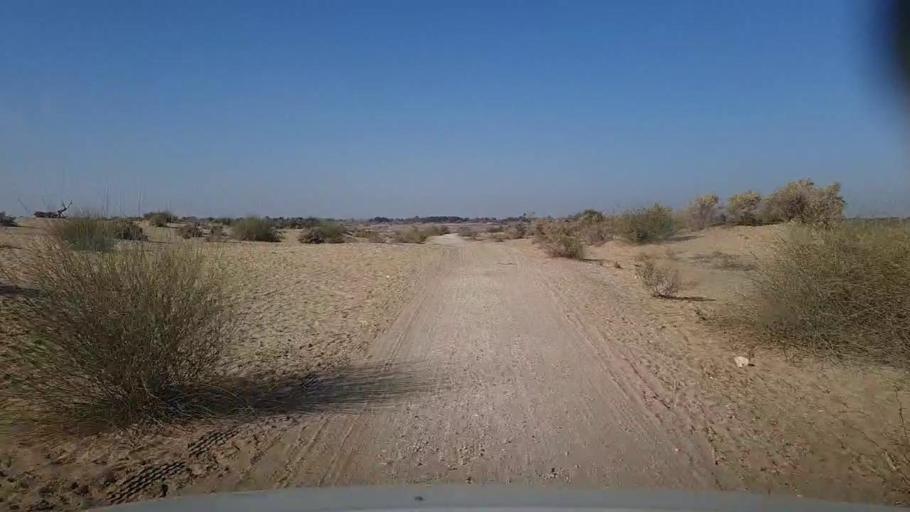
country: PK
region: Sindh
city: Khairpur
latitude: 27.9618
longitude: 69.8118
